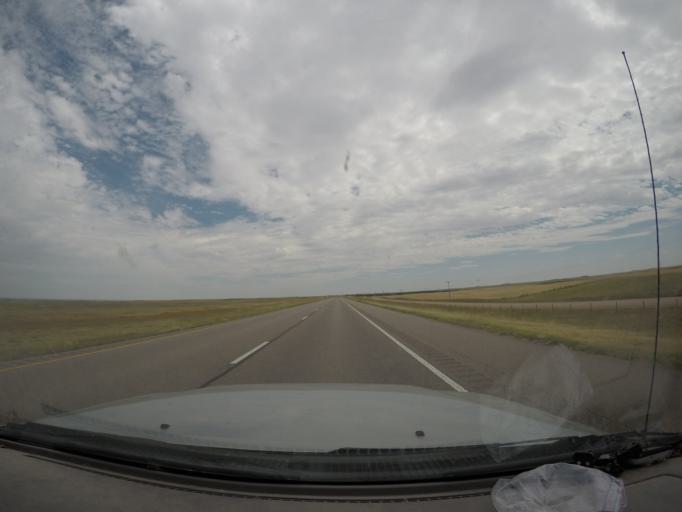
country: US
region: Nebraska
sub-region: Kimball County
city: Kimball
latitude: 41.1918
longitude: -103.7887
